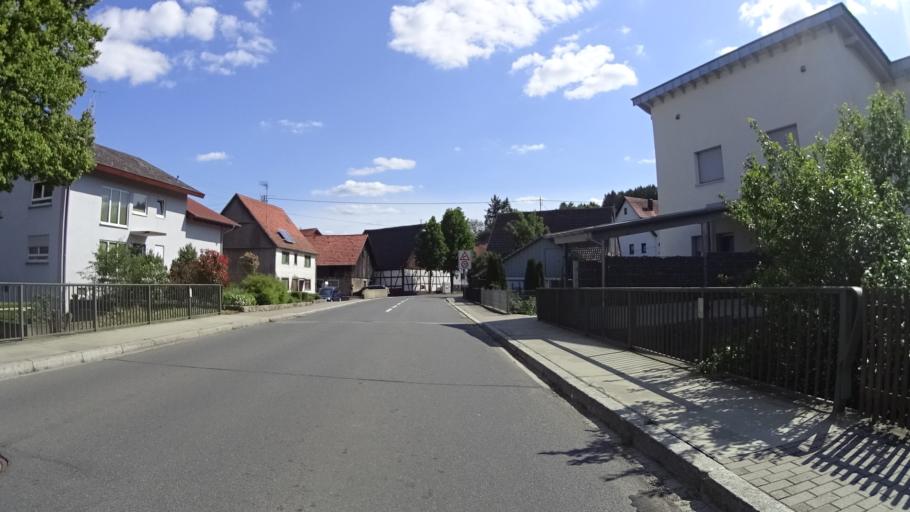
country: DE
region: Baden-Wuerttemberg
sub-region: Regierungsbezirk Stuttgart
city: Buch am Ahorn
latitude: 49.5550
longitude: 9.4968
